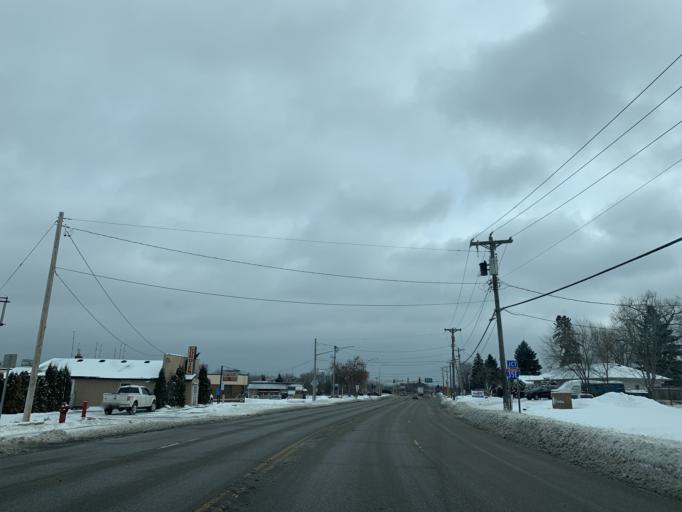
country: US
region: Minnesota
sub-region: Ramsey County
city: Little Canada
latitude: 45.0238
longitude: -93.0931
